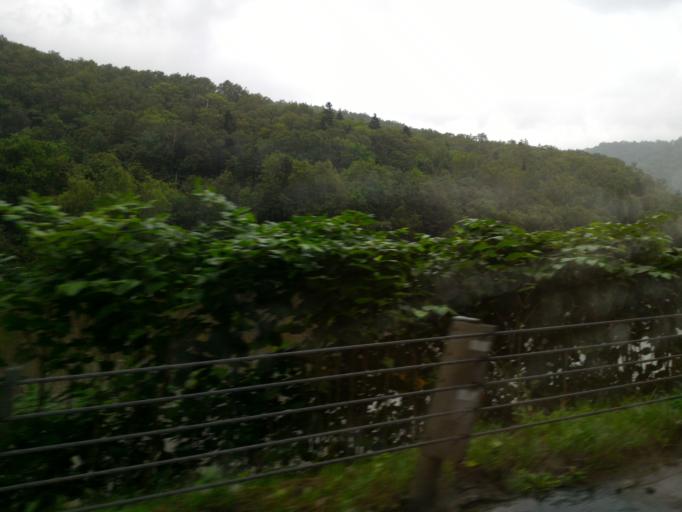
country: JP
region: Hokkaido
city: Nayoro
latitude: 44.7250
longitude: 142.1677
